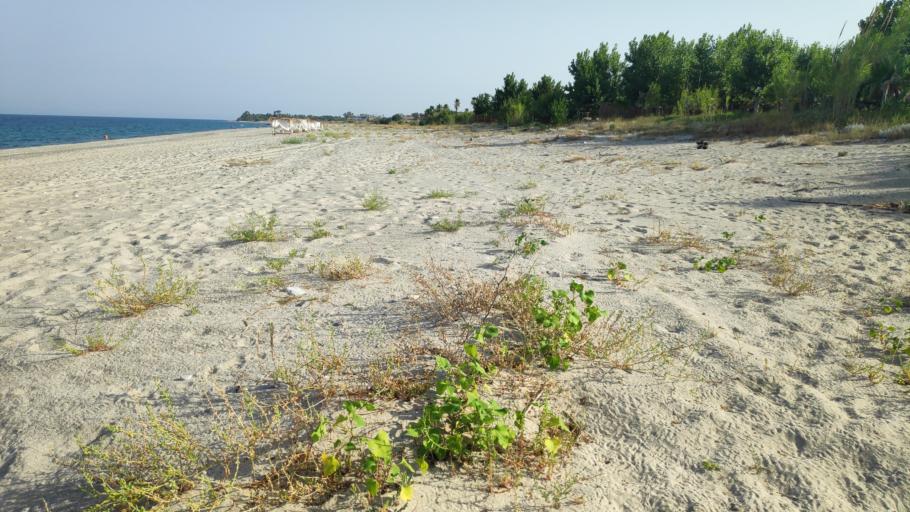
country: IT
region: Calabria
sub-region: Provincia di Catanzaro
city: Santa Caterina dello Ionio Marina
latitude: 38.5155
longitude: 16.5743
